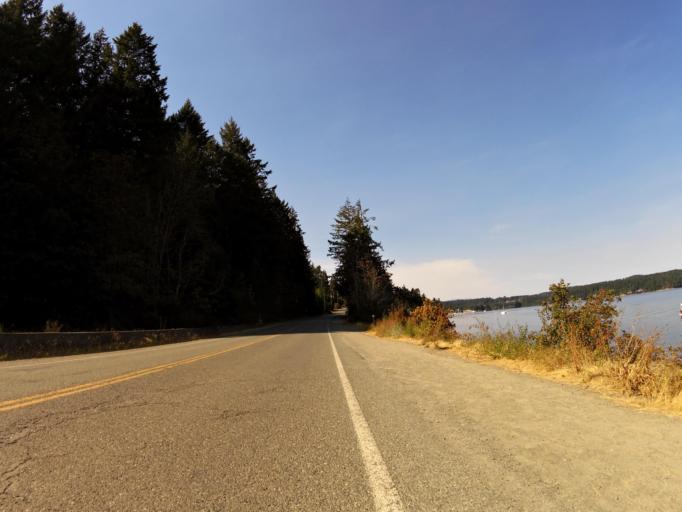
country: CA
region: British Columbia
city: North Saanich
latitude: 48.6355
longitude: -123.5353
